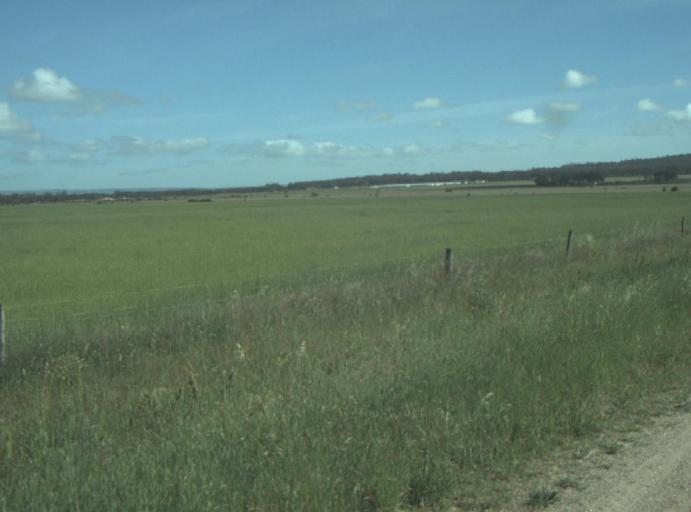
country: AU
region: Victoria
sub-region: Greater Geelong
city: Lara
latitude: -37.9852
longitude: 144.4219
